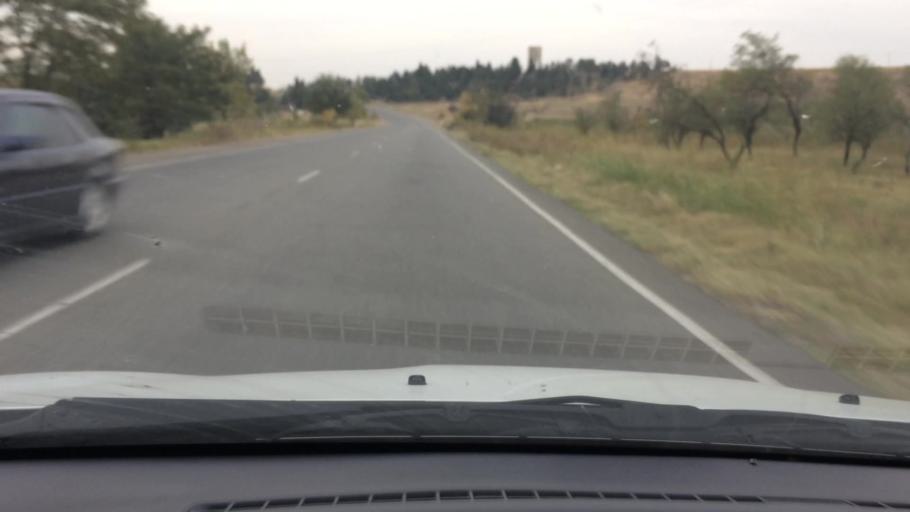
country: GE
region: Kvemo Kartli
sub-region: Marneuli
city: Marneuli
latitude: 41.5286
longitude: 44.7770
